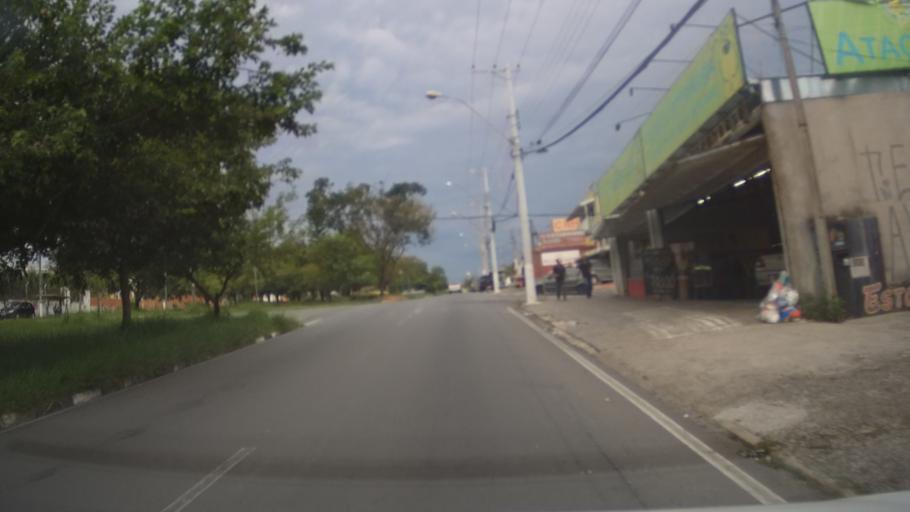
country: BR
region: Sao Paulo
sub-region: Campinas
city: Campinas
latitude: -22.9304
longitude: -47.1040
